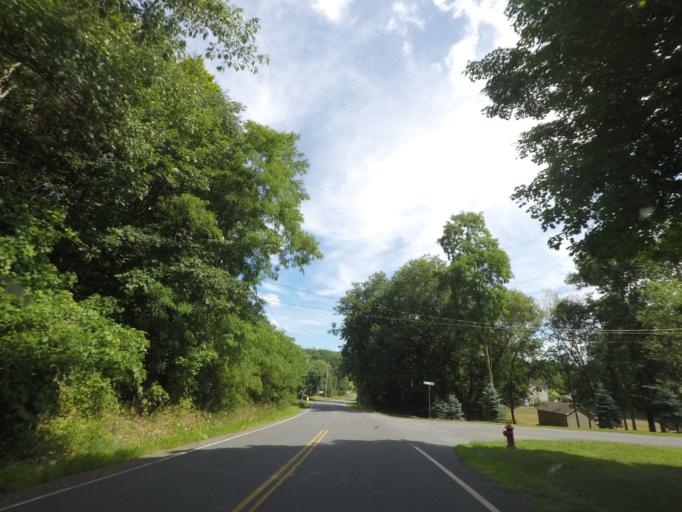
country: US
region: New York
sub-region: Rensselaer County
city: Wynantskill
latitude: 42.7010
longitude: -73.6089
